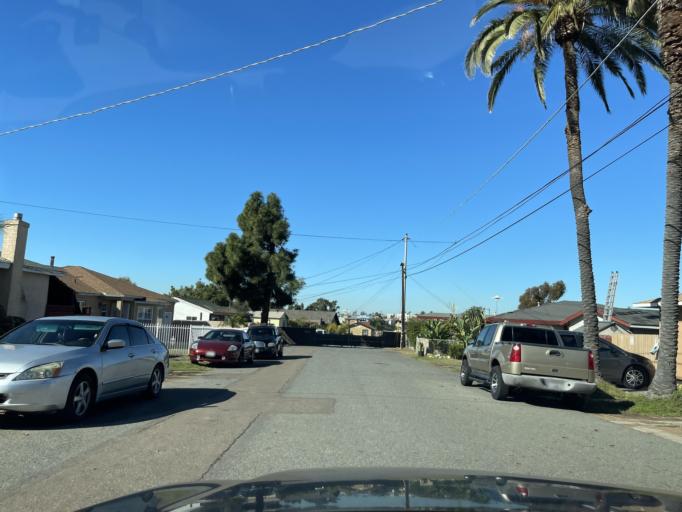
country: US
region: California
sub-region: San Diego County
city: National City
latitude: 32.6759
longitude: -117.0901
